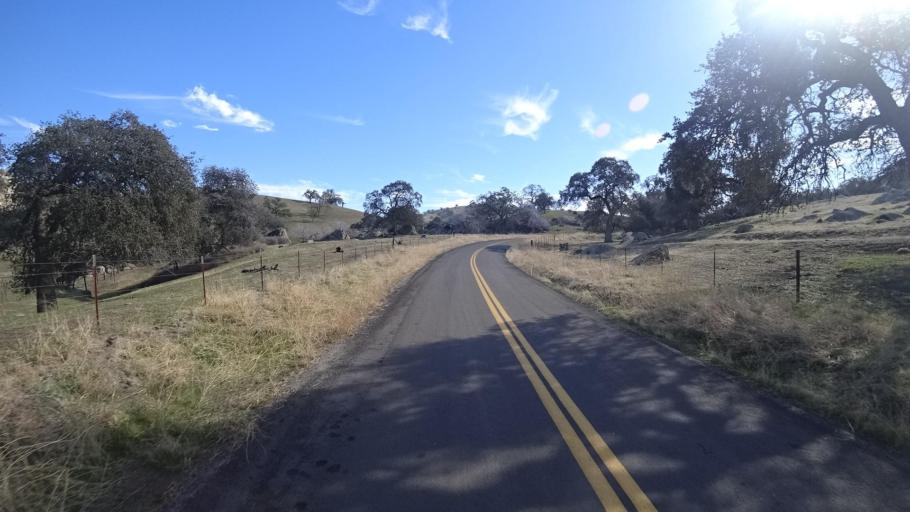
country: US
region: California
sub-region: Tulare County
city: Richgrove
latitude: 35.6704
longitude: -118.8503
